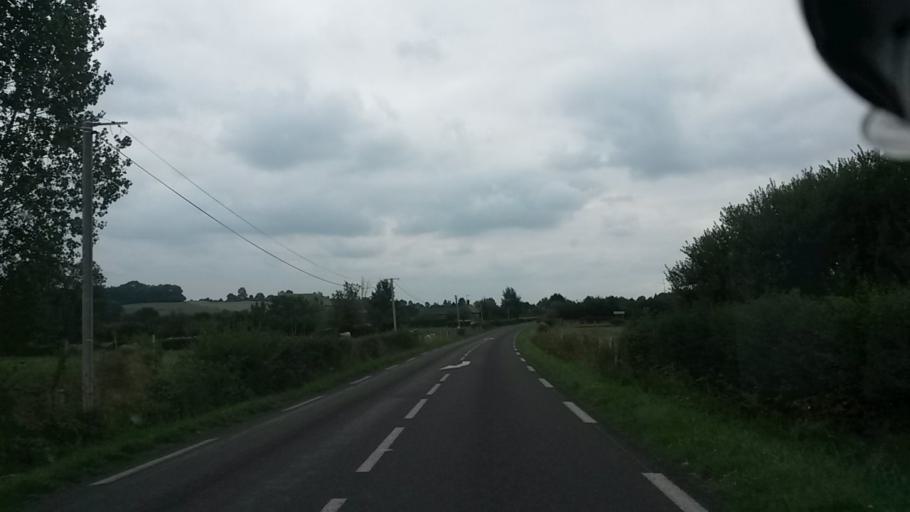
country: FR
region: Haute-Normandie
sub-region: Departement de la Seine-Maritime
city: Forges-les-Eaux
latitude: 49.5770
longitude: 1.5423
